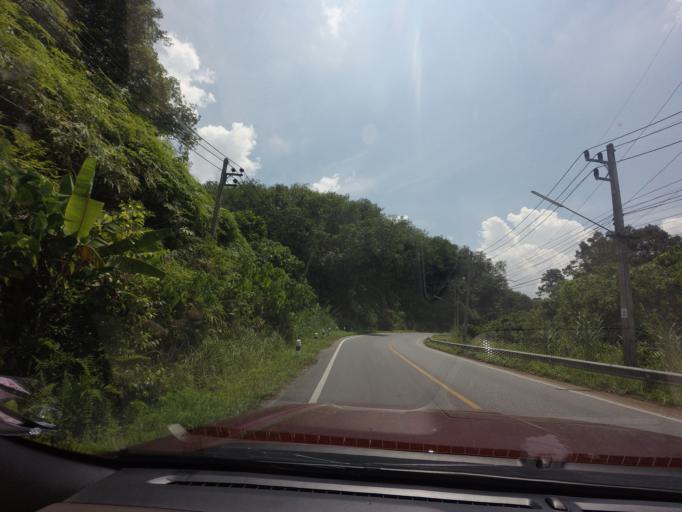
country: TH
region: Yala
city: Betong
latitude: 5.8864
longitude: 101.1455
